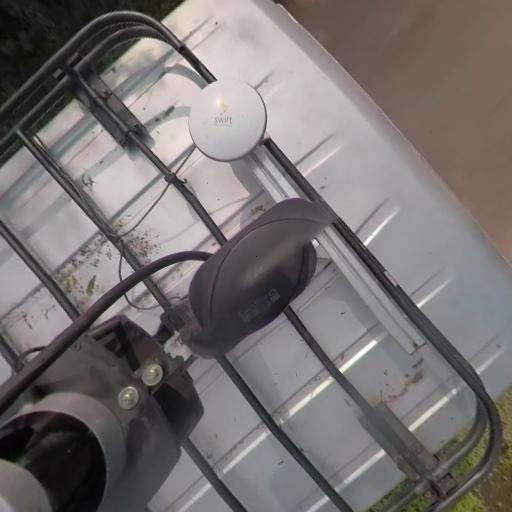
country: IN
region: Telangana
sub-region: Nalgonda
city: Suriapet
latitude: 17.2018
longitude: 79.4867
